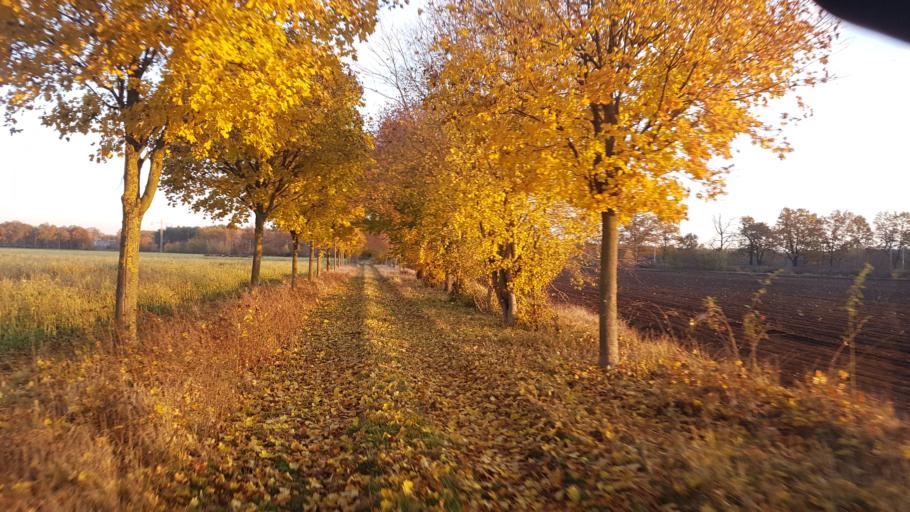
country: DE
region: Brandenburg
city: Schilda
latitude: 51.5895
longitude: 13.3227
